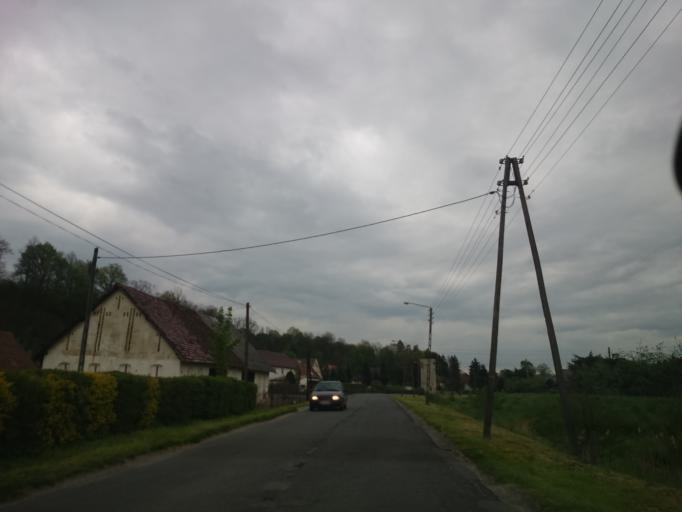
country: PL
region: Lower Silesian Voivodeship
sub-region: Powiat klodzki
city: Klodzko
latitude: 50.4191
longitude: 16.6688
